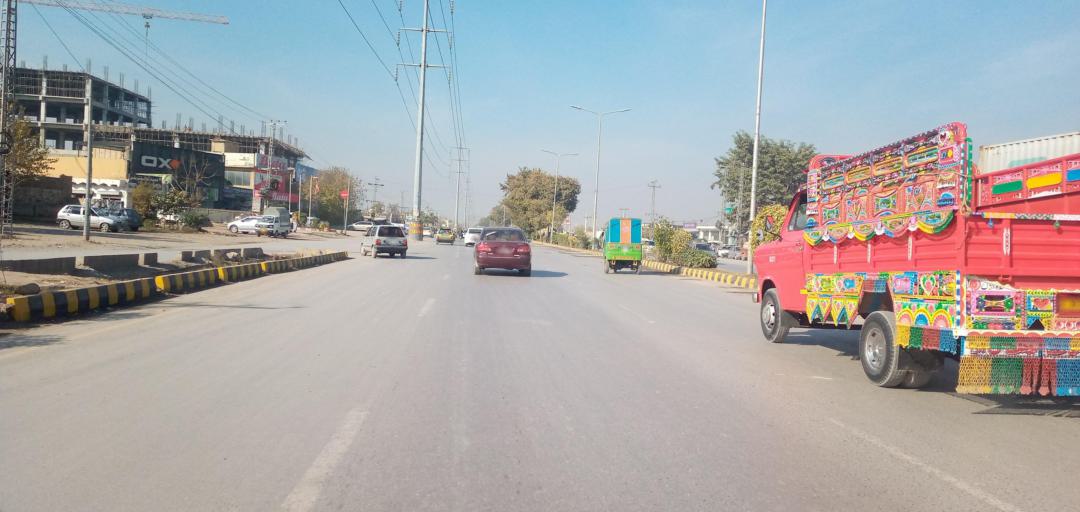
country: PK
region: Khyber Pakhtunkhwa
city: Peshawar
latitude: 33.9626
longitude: 71.5017
